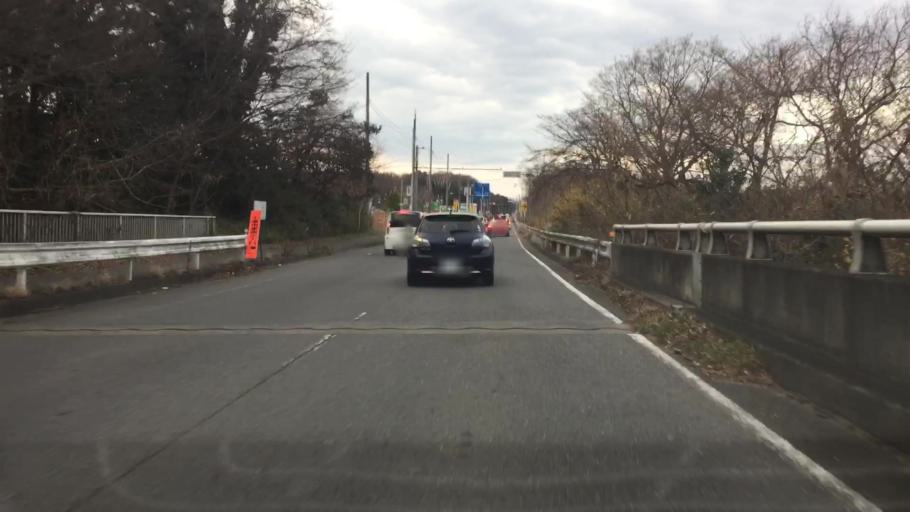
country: JP
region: Chiba
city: Shiroi
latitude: 35.7837
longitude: 140.0184
